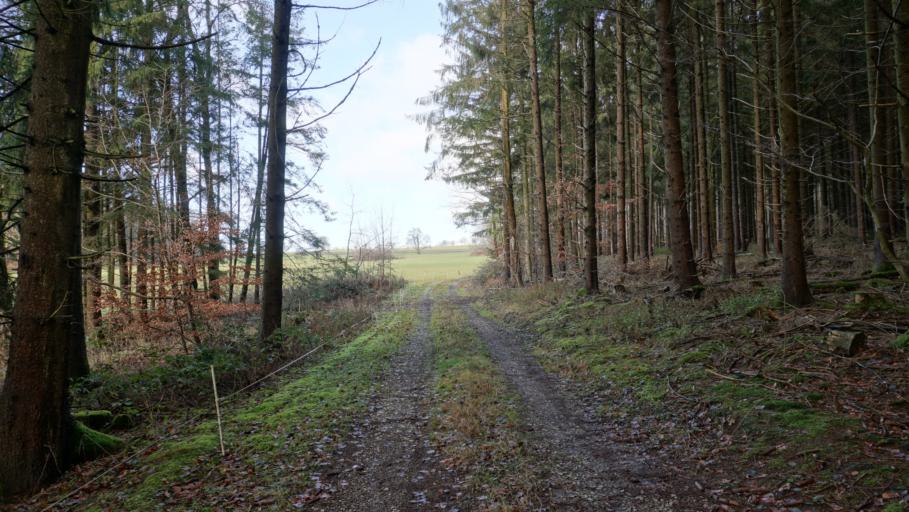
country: DE
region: Baden-Wuerttemberg
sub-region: Karlsruhe Region
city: Fahrenbach
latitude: 49.4346
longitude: 9.1118
